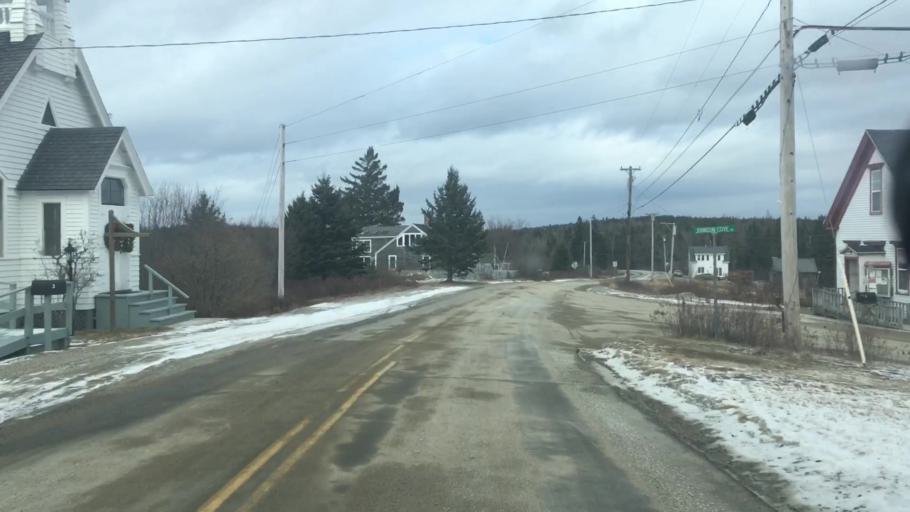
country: US
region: Maine
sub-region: Washington County
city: Machias
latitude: 44.6130
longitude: -67.4802
